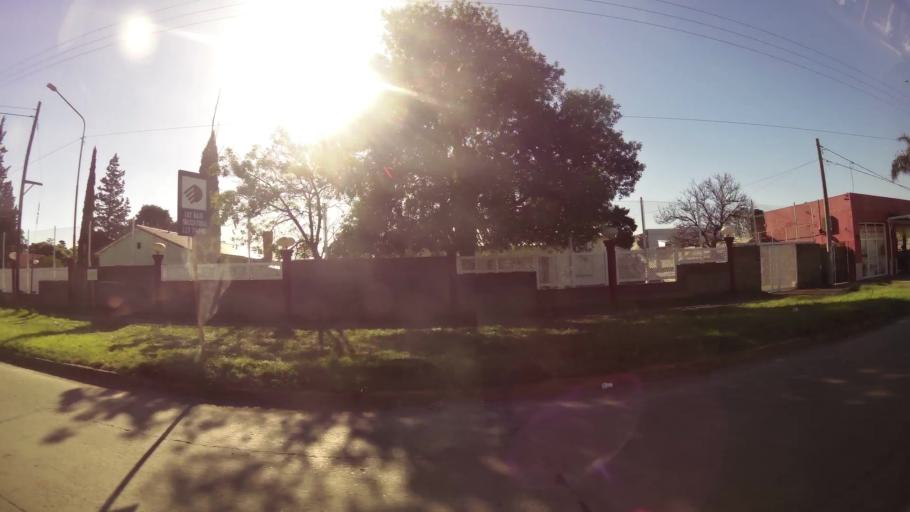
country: AR
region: Cordoba
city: San Francisco
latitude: -31.4256
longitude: -62.0965
